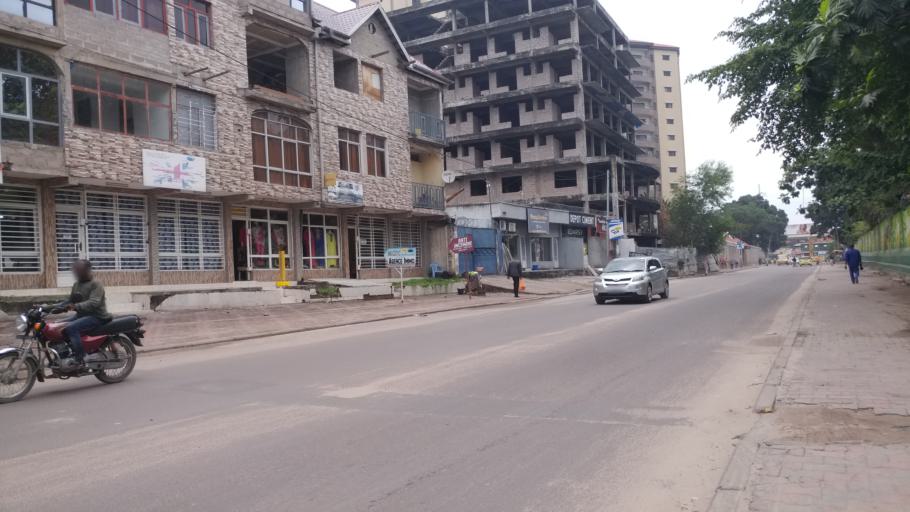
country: CD
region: Kinshasa
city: Kinshasa
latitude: -4.3220
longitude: 15.2764
